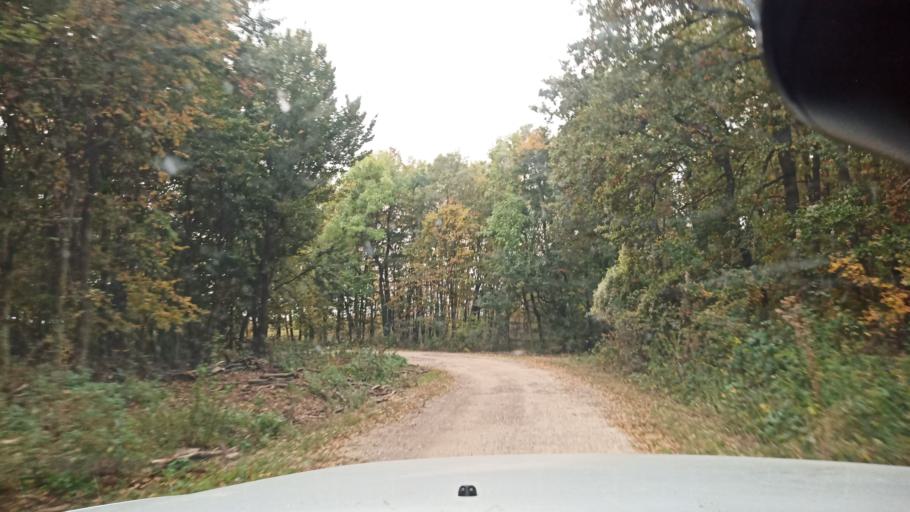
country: HU
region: Fejer
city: Bodajk
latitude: 47.3779
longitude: 18.2730
